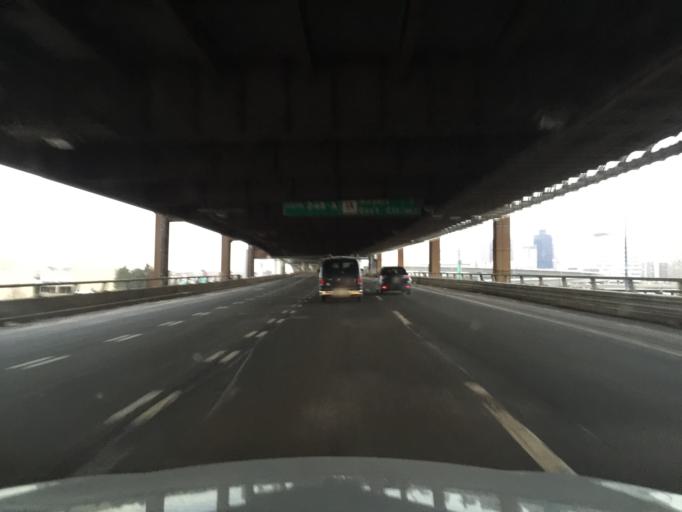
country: US
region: Massachusetts
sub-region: Suffolk County
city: Boston
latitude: 42.3748
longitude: -71.0723
